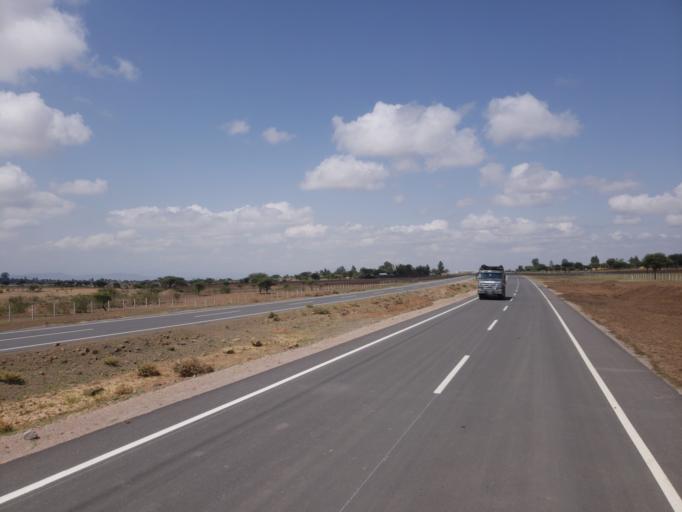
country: ET
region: Oromiya
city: Mojo
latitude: 8.5459
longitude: 39.1031
